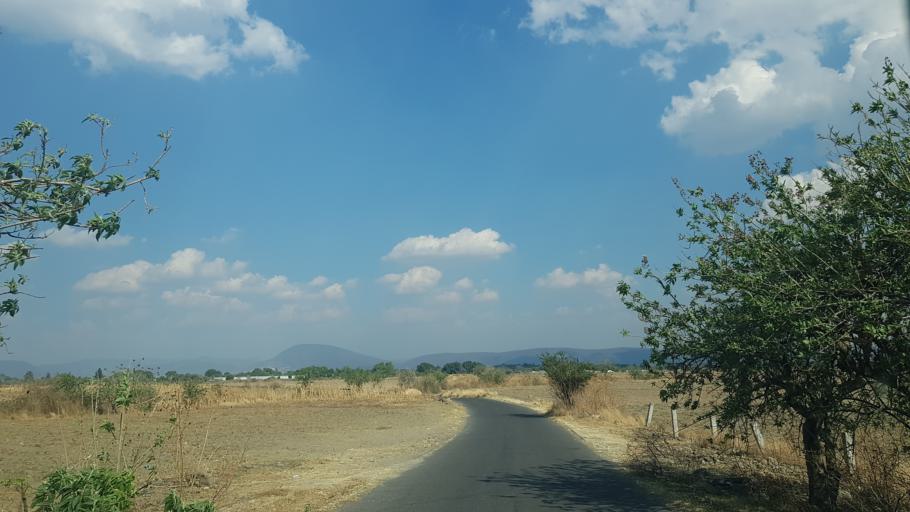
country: MX
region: Puebla
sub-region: Atlixco
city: Colonia Agricola de Ocotepec (Colonia San Jose)
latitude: 18.8865
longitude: -98.4974
